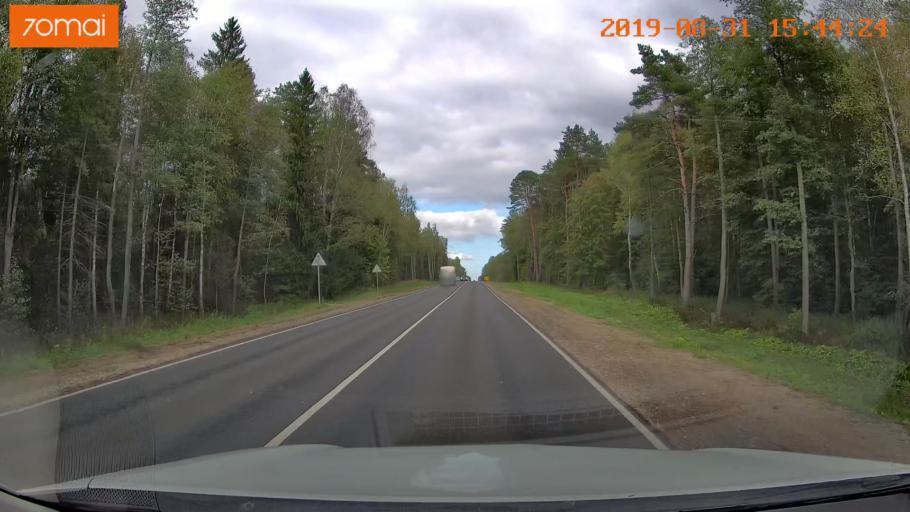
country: RU
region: Kaluga
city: Mosal'sk
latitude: 54.6589
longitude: 34.9323
